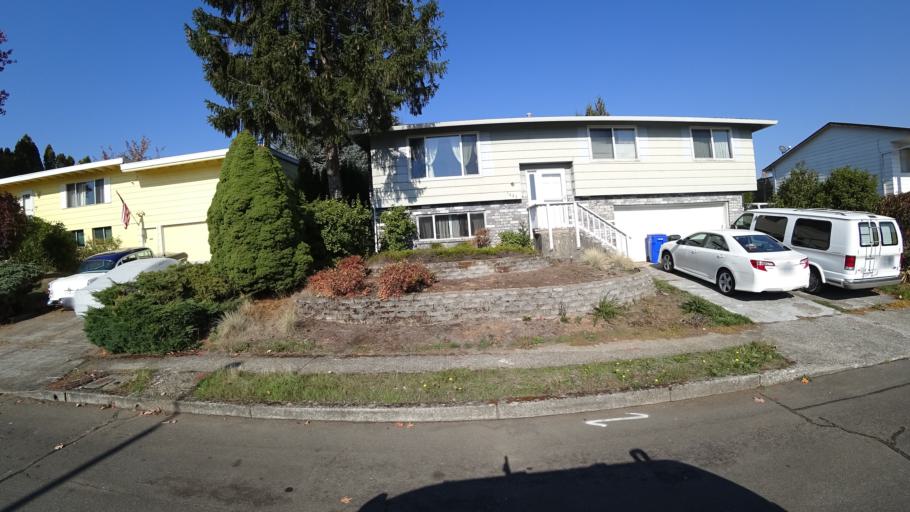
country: US
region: Oregon
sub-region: Multnomah County
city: Gresham
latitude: 45.4946
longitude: -122.4462
